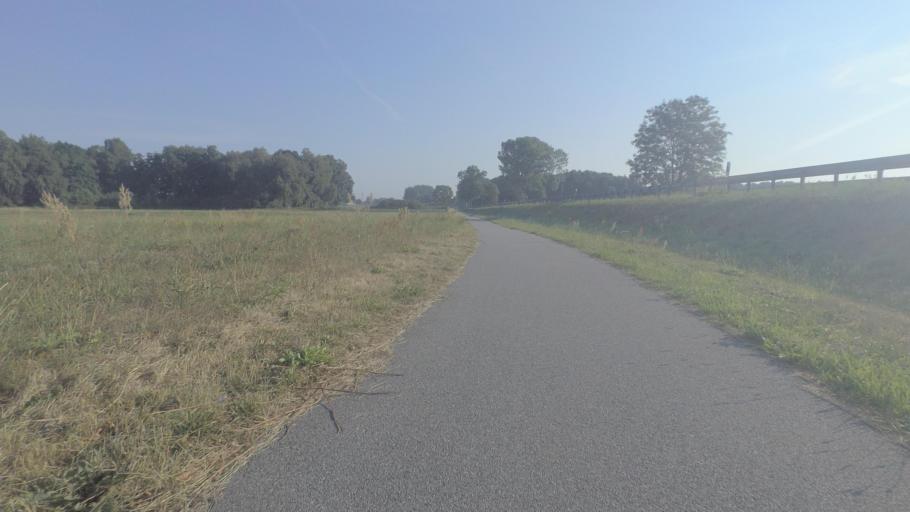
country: DE
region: Mecklenburg-Vorpommern
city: Tutow
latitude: 53.9797
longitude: 13.1481
